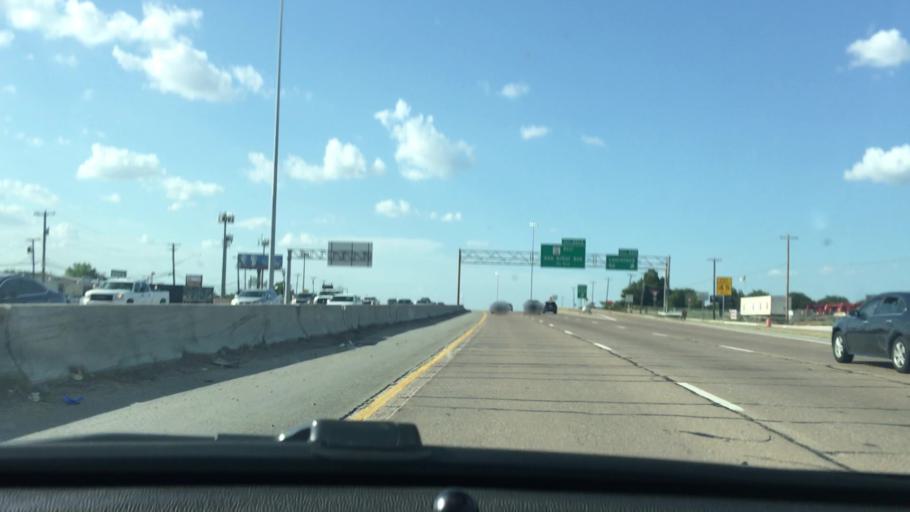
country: US
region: Texas
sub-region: Dallas County
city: DeSoto
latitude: 32.6700
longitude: -96.8226
